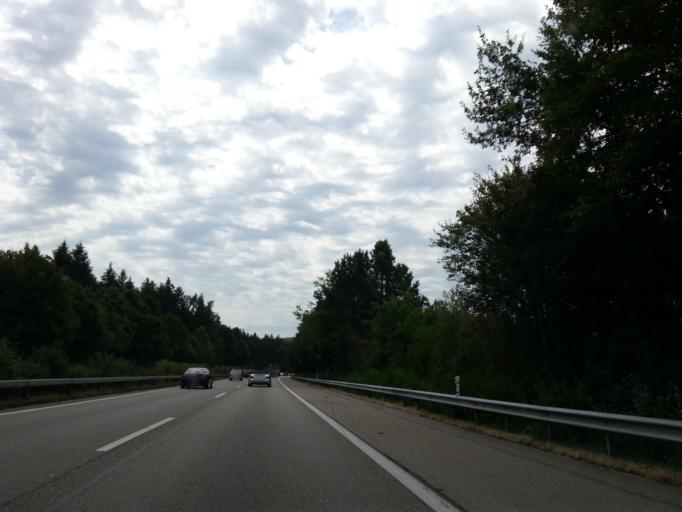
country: CH
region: Bern
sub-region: Emmental District
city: Hindelbank
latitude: 47.0381
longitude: 7.5287
